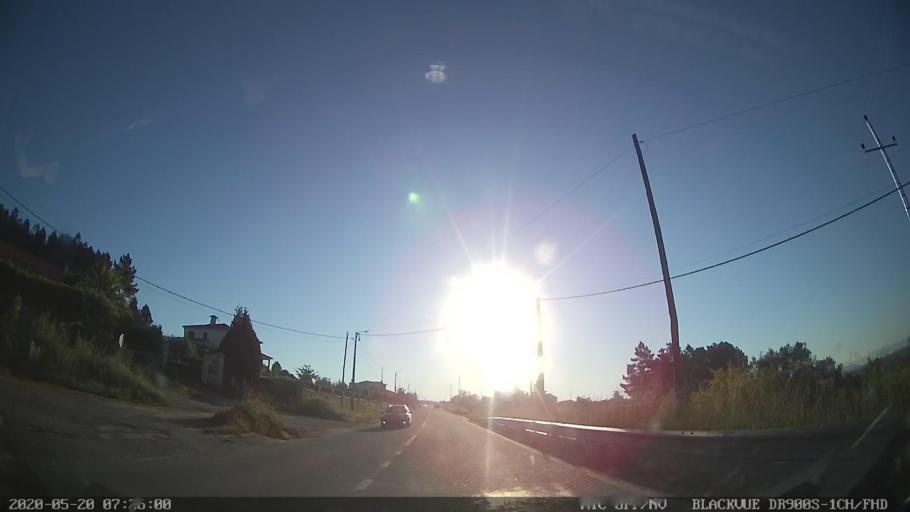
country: PT
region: Vila Real
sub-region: Sabrosa
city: Sabrosa
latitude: 41.2604
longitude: -7.6007
